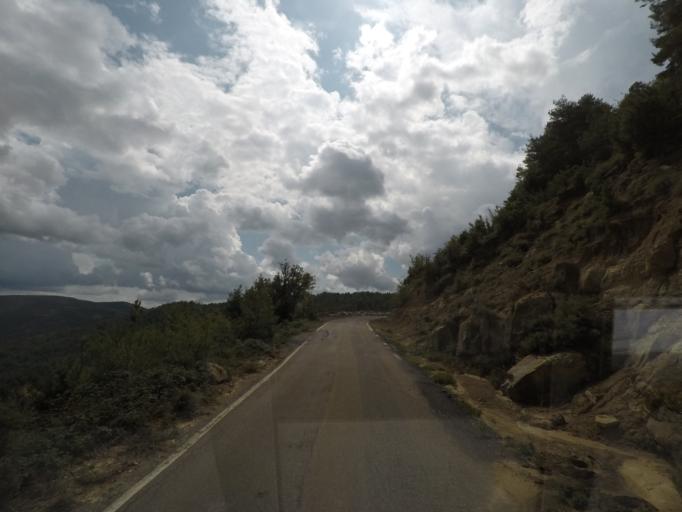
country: ES
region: Aragon
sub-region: Provincia de Huesca
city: Boltana
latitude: 42.4013
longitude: -0.0101
